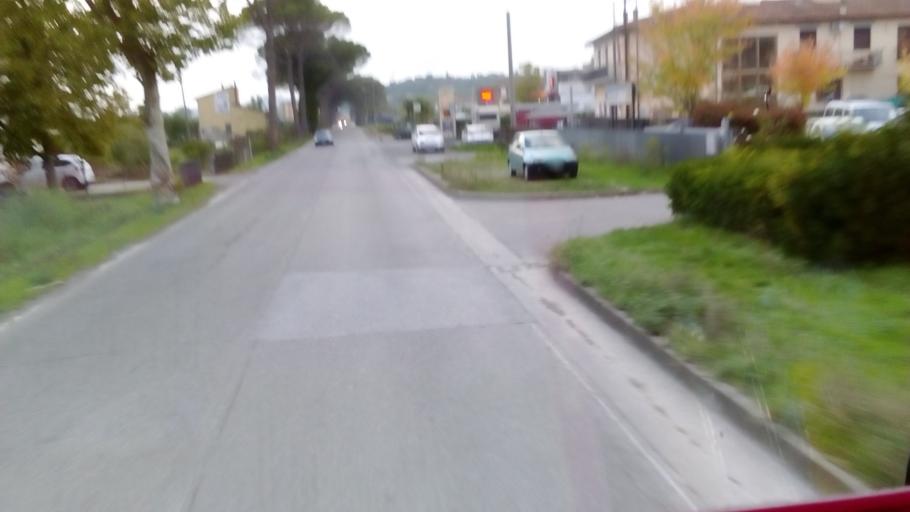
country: IT
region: Tuscany
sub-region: Province of Florence
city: Castelfiorentino
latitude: 43.6241
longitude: 10.9616
